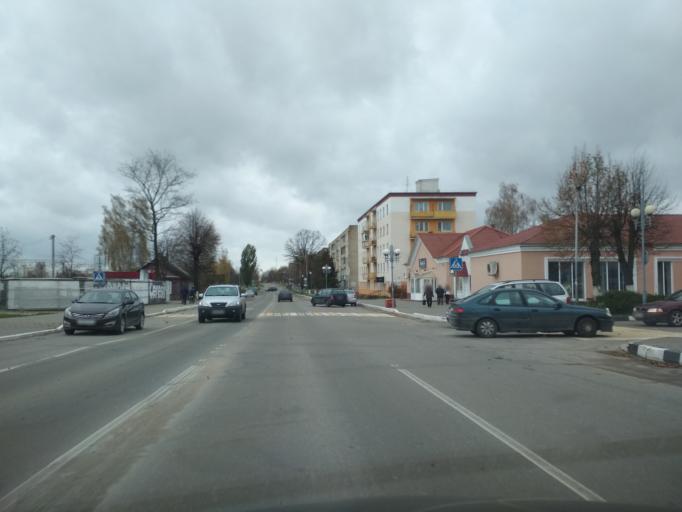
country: BY
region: Minsk
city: Mar''ina Horka
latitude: 53.5109
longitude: 28.1438
